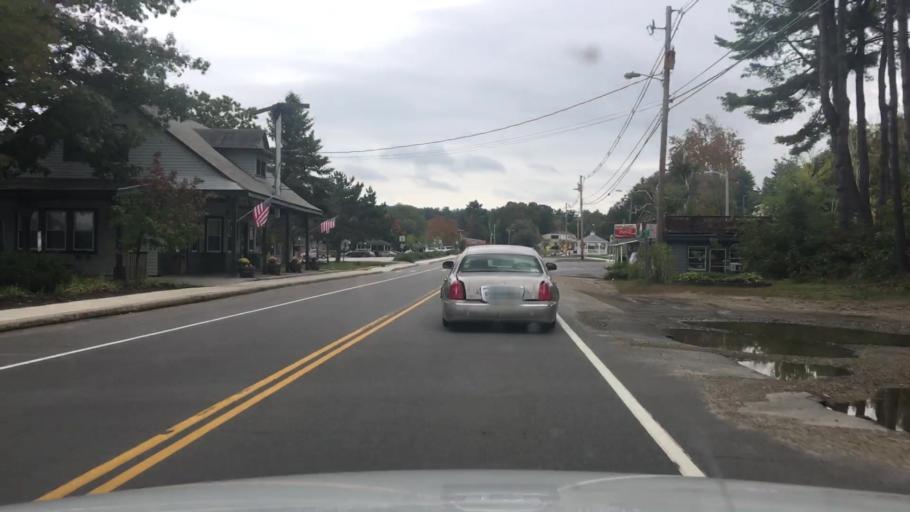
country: US
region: New Hampshire
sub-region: Strafford County
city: New Durham
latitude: 43.4736
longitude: -71.2380
